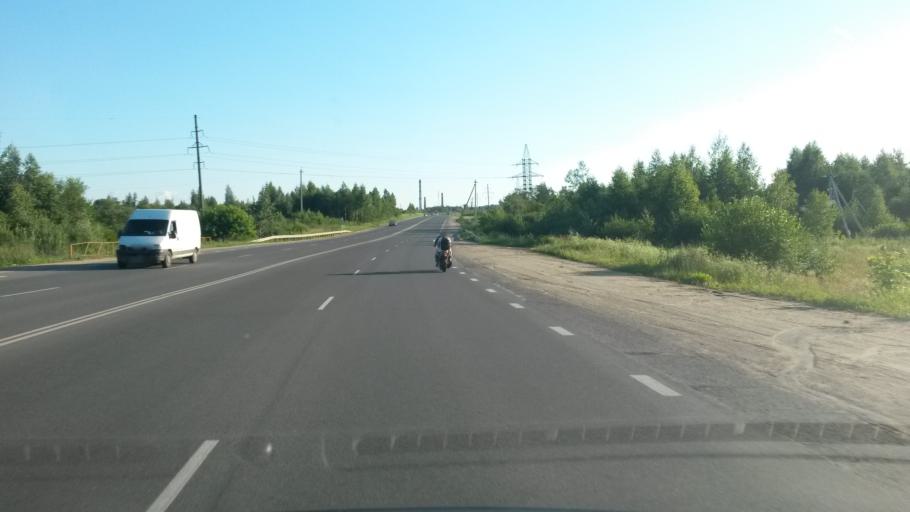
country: RU
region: Ivanovo
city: Novo-Talitsy
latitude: 57.0149
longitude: 40.8852
